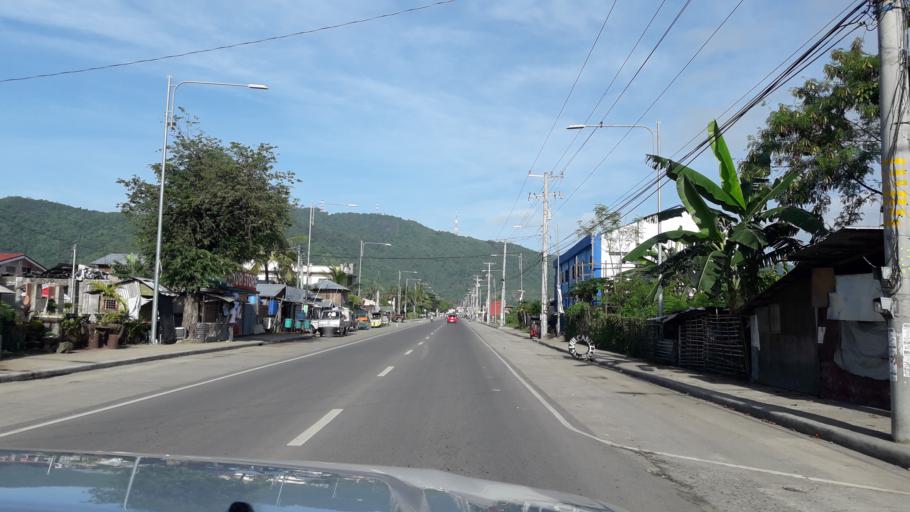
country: PH
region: Eastern Visayas
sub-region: Province of Leyte
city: Pawing
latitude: 11.2150
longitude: 125.0002
